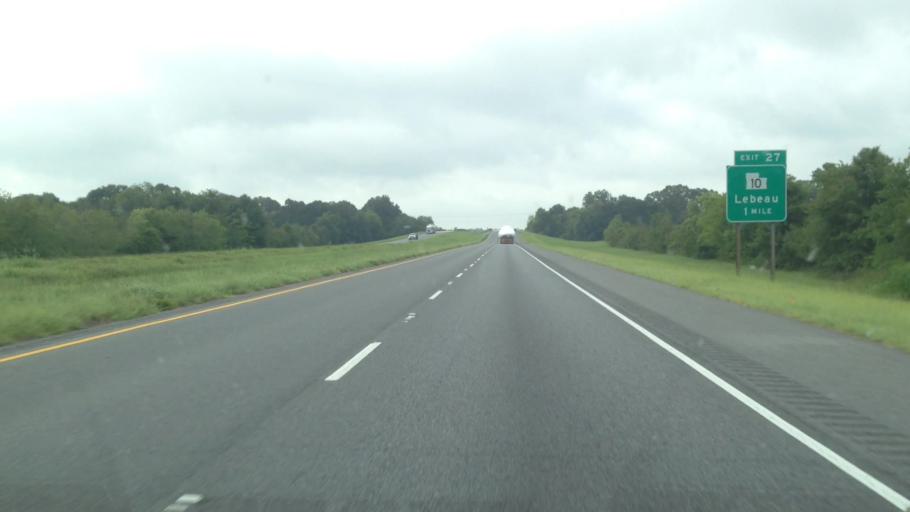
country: US
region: Louisiana
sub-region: Saint Landry Parish
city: Opelousas
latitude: 30.6574
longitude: -92.0632
